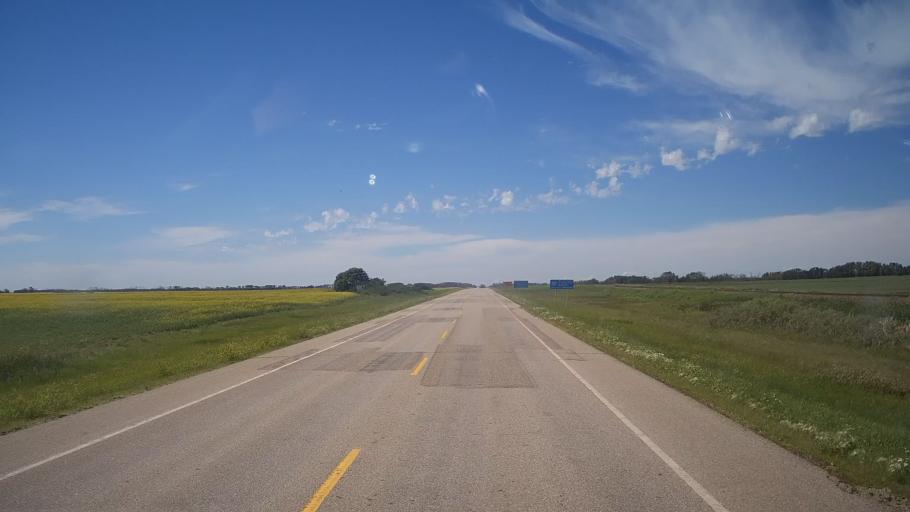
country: CA
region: Saskatchewan
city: Langenburg
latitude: 50.7800
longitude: -101.5170
